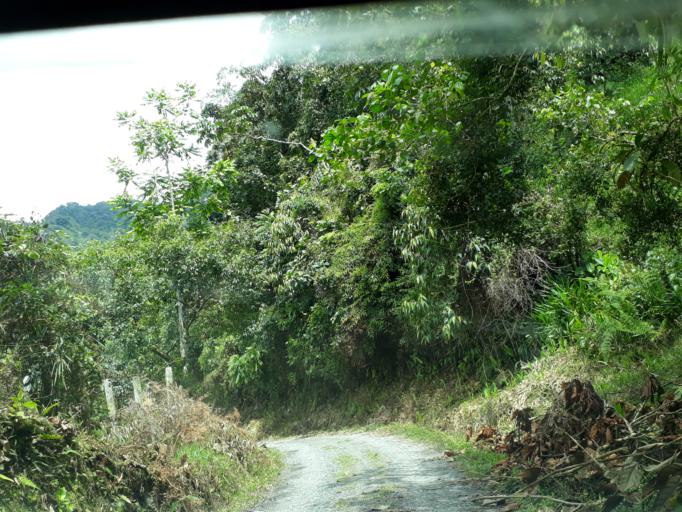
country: CO
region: Cundinamarca
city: Topaipi
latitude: 5.3113
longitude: -74.2097
